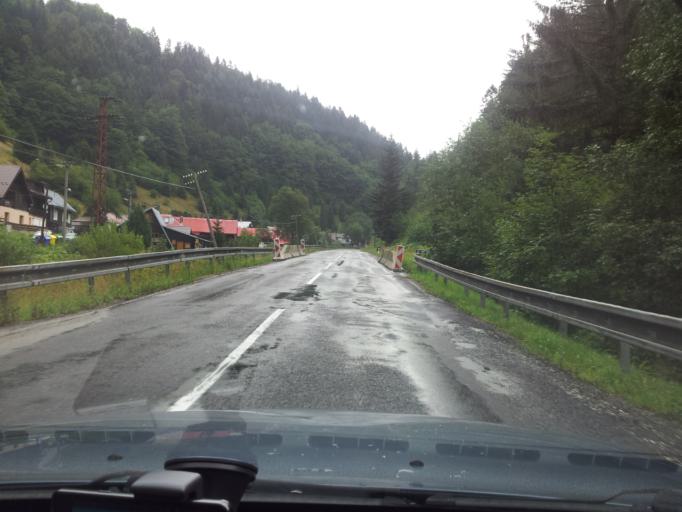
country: SK
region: Banskobystricky
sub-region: Okres Banska Bystrica
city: Brezno
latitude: 48.8925
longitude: 19.6931
